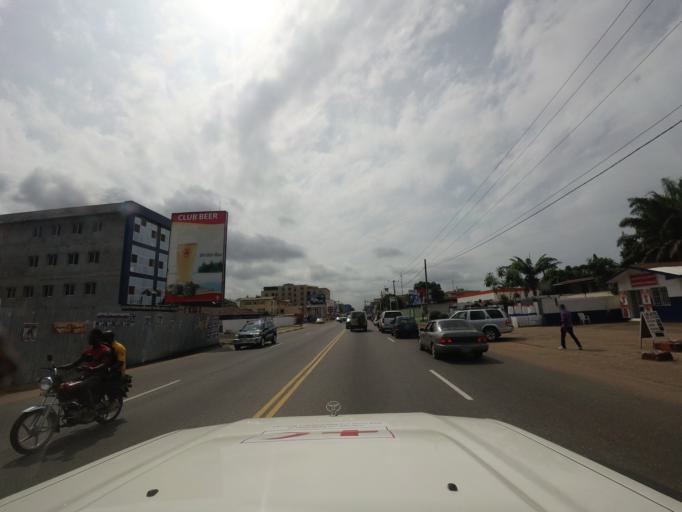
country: LR
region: Montserrado
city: Monrovia
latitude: 6.2932
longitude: -10.7830
